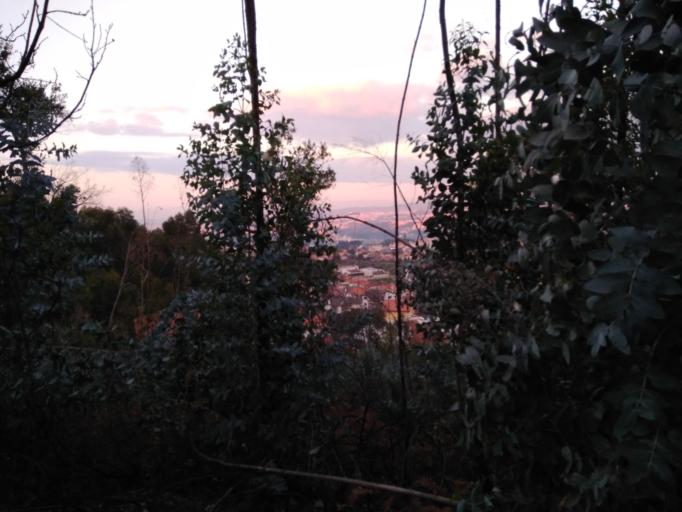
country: PT
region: Porto
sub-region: Vila Nova de Gaia
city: Vilar de Andorinho
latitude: 41.1032
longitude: -8.5833
